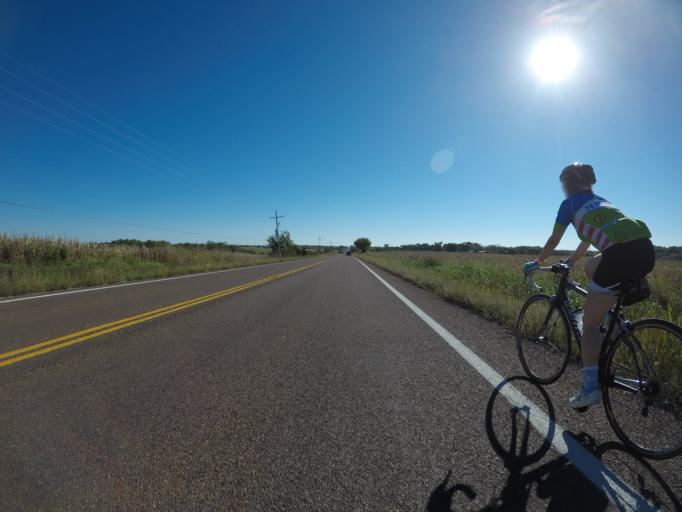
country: US
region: Kansas
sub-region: Johnson County
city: De Soto
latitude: 39.0582
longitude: -94.9701
